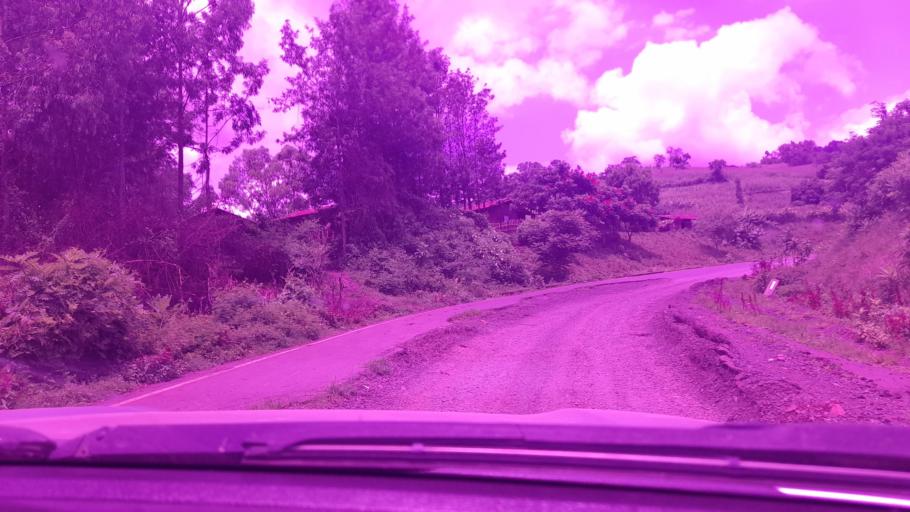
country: ET
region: Oromiya
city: Metu
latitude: 8.3270
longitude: 35.7595
